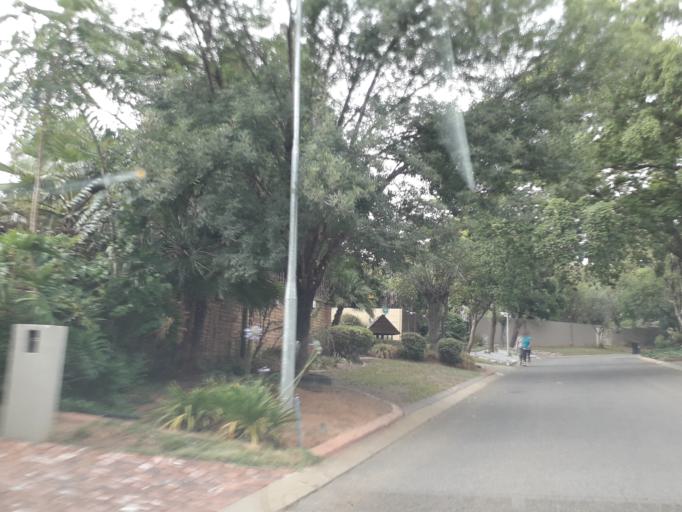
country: ZA
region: Gauteng
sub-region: City of Johannesburg Metropolitan Municipality
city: Roodepoort
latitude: -26.1038
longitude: 27.9590
